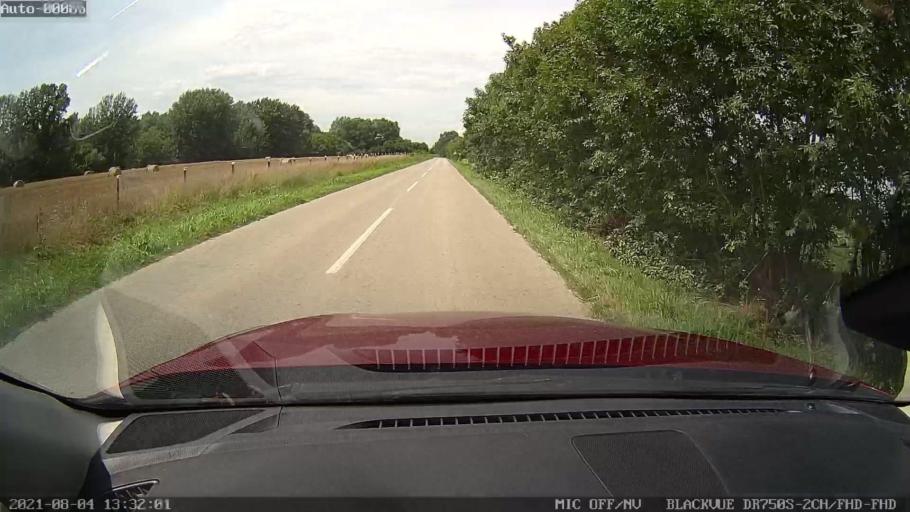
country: HR
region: Osjecko-Baranjska
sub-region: Grad Osijek
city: Bilje
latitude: 45.6062
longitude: 18.7655
